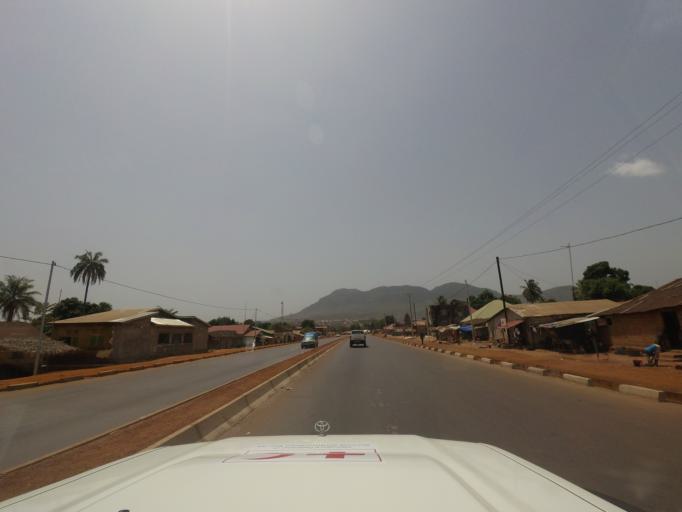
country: GN
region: Kindia
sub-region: Coyah
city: Coyah
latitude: 9.7203
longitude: -13.4126
